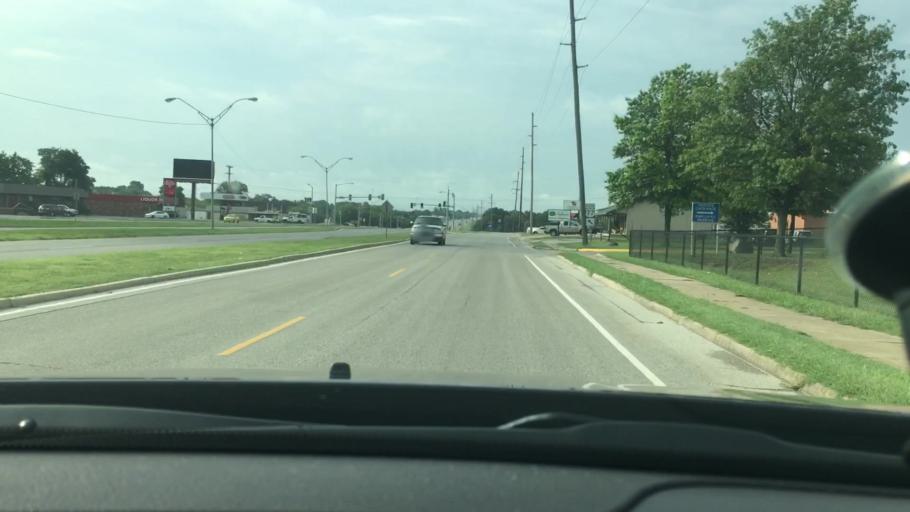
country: US
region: Oklahoma
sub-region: Carter County
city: Ardmore
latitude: 34.1604
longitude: -97.1435
